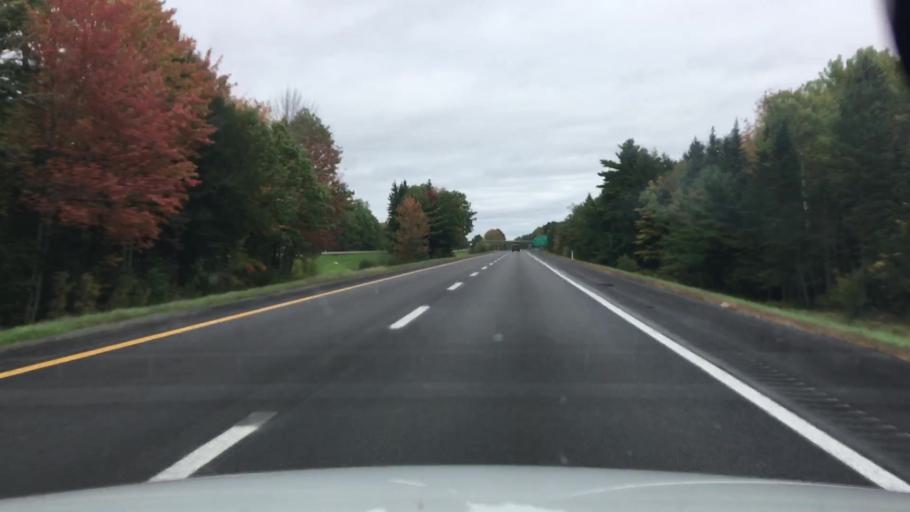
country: US
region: Maine
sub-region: Penobscot County
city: Orono
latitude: 44.8843
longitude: -68.6954
